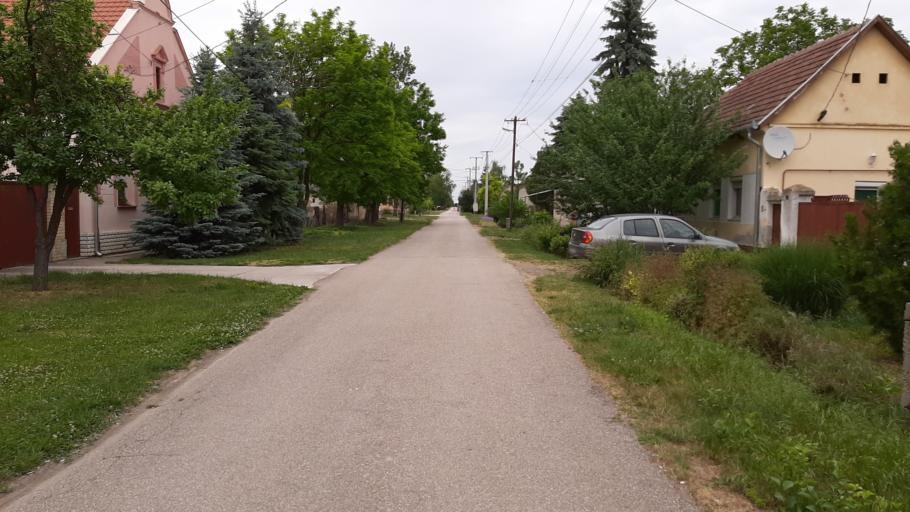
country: RO
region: Timis
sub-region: Comuna Beba Veche
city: Beba Veche
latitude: 46.1480
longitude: 20.2785
